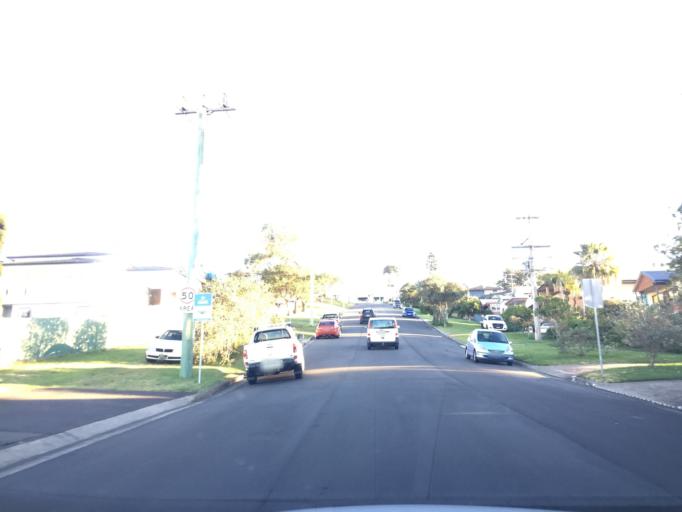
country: AU
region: New South Wales
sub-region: Kiama
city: Kiama
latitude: -34.6636
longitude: 150.8515
